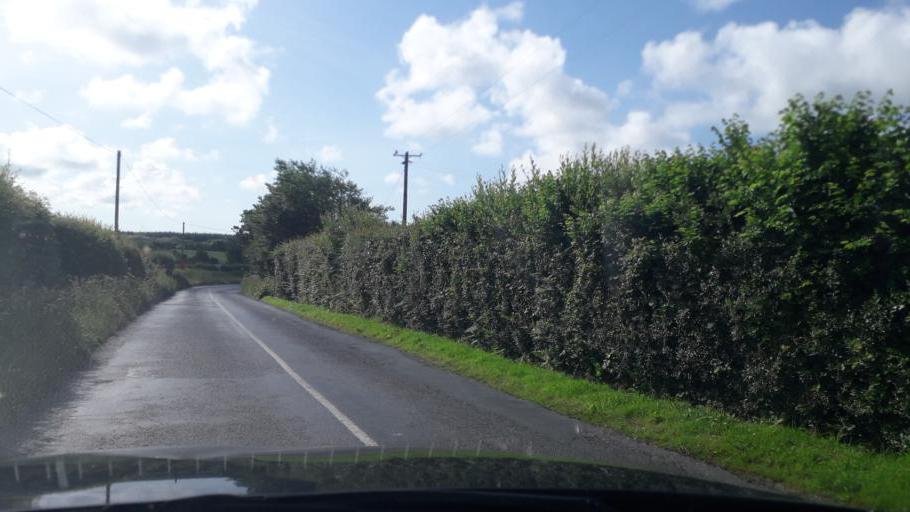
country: IE
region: Leinster
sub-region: Loch Garman
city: Loch Garman
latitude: 52.2645
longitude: -6.5580
